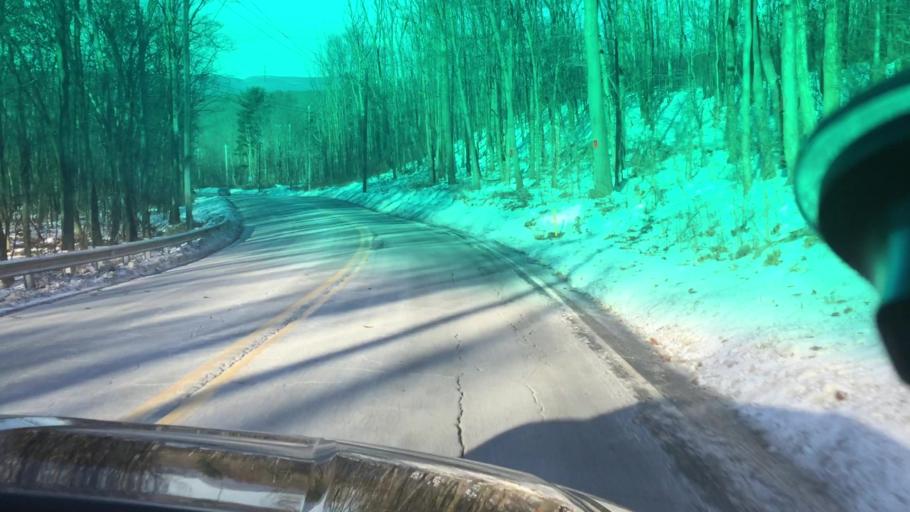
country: US
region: Pennsylvania
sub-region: Luzerne County
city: Freeland
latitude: 41.0793
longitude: -75.9580
